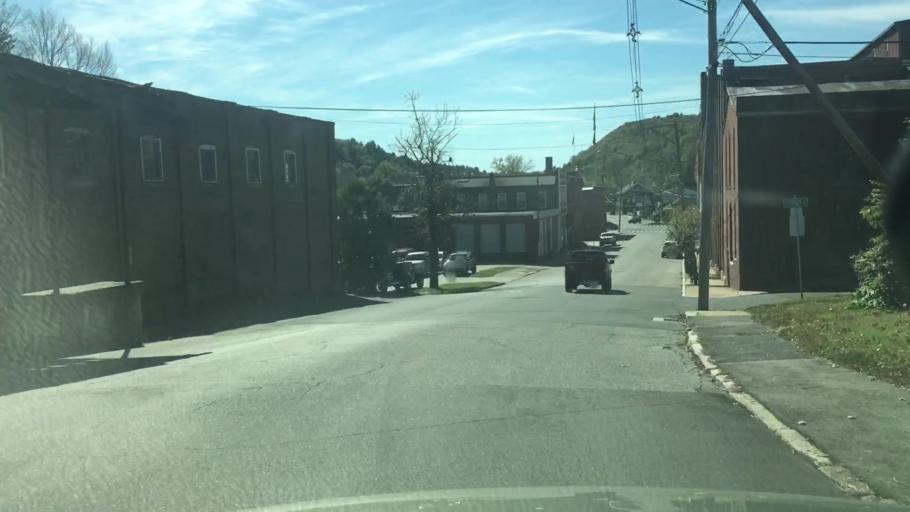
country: US
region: Connecticut
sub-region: Tolland County
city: Stafford Springs
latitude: 41.9555
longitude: -72.3022
